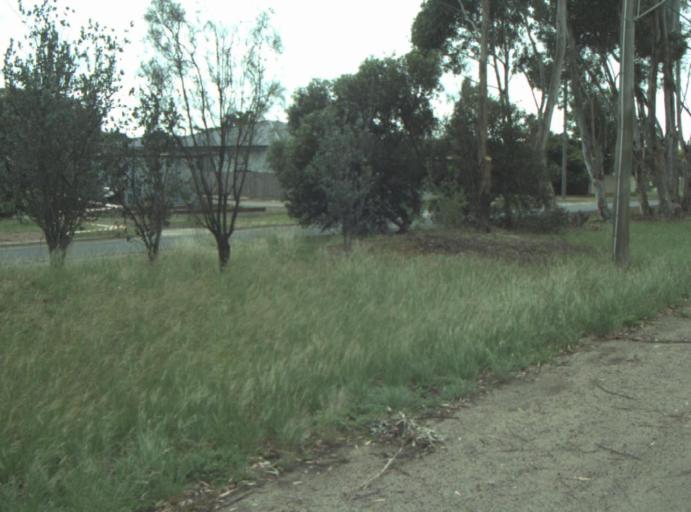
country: AU
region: Victoria
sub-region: Greater Geelong
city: Lara
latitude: -38.0255
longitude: 144.4216
